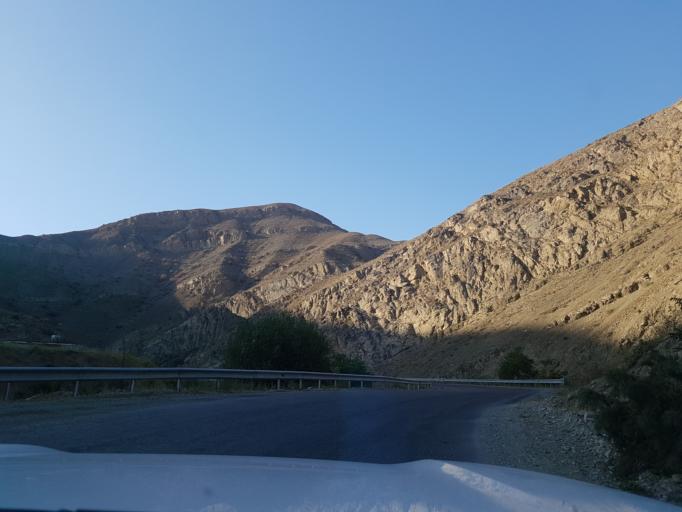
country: TM
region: Ahal
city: Baharly
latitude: 38.4948
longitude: 57.0465
